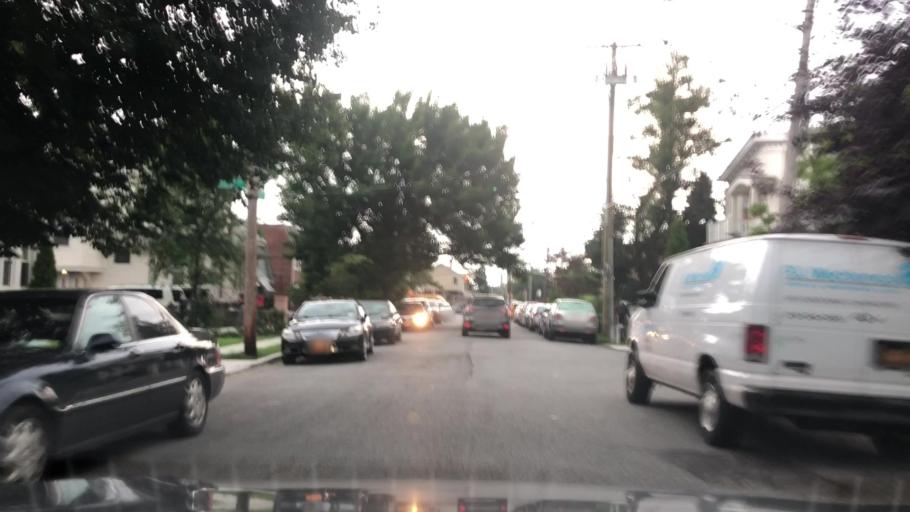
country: US
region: New York
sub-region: Nassau County
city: Bellerose Terrace
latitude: 40.7135
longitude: -73.7325
